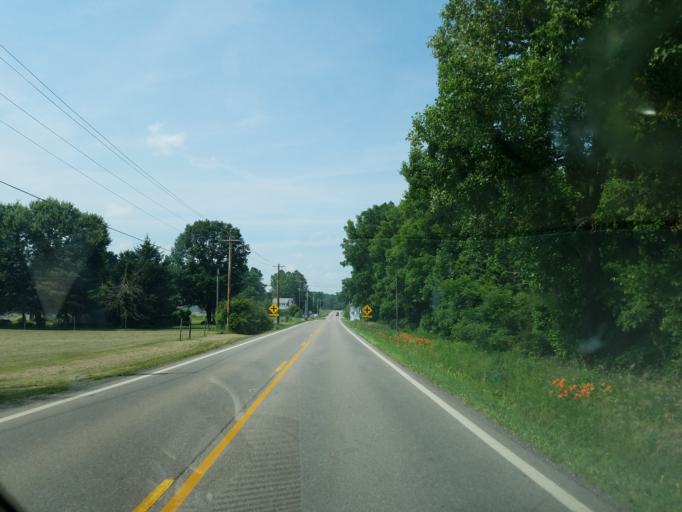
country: US
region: Ohio
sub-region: Licking County
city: Utica
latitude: 40.1741
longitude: -82.5192
